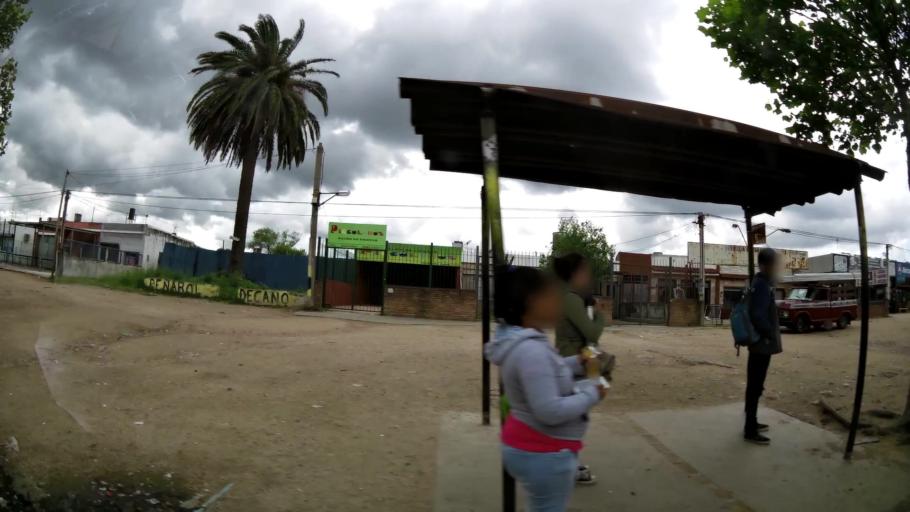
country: UY
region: Canelones
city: Toledo
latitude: -34.8219
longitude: -56.1402
